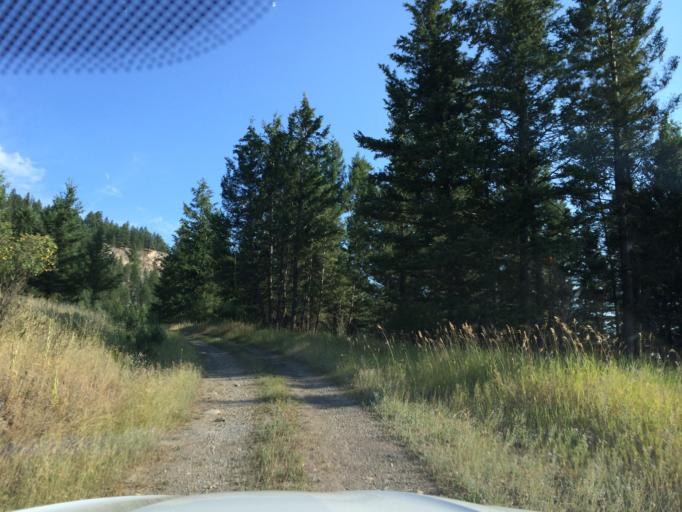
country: US
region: Montana
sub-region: Lincoln County
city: Eureka
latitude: 49.0003
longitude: -115.0523
